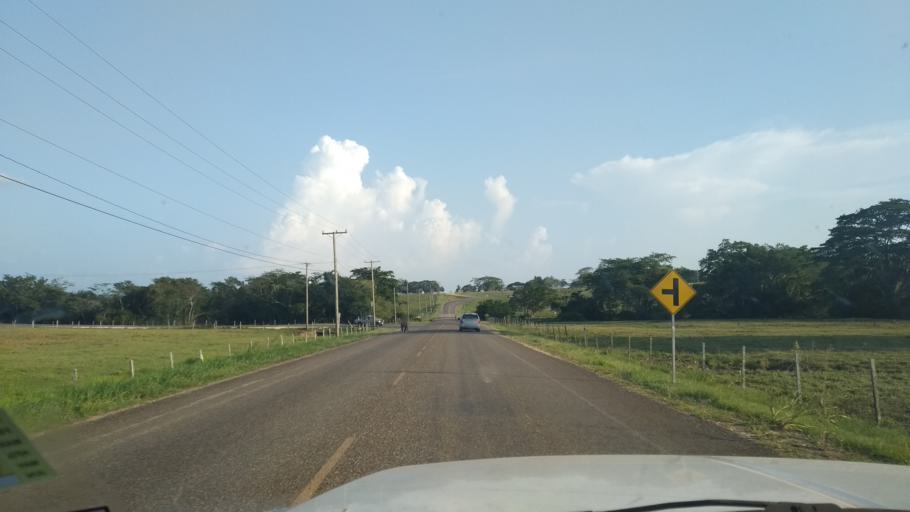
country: BZ
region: Cayo
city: San Ignacio
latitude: 17.2491
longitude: -88.9874
